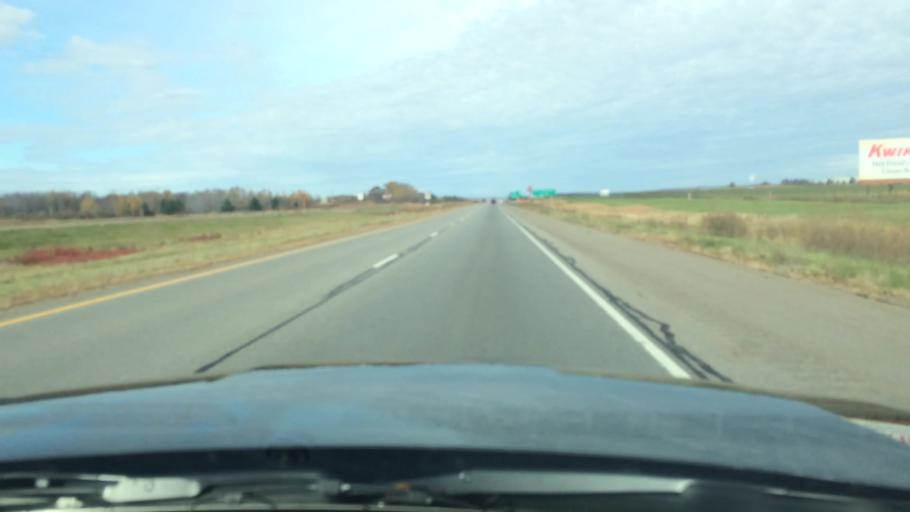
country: US
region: Wisconsin
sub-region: Marathon County
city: Mosinee
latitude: 44.7767
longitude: -89.6801
